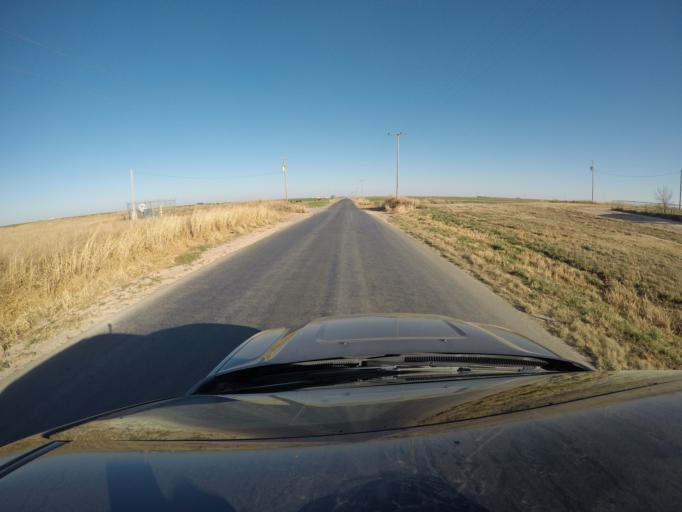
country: US
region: New Mexico
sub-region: Curry County
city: Texico
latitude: 34.3028
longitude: -103.1093
